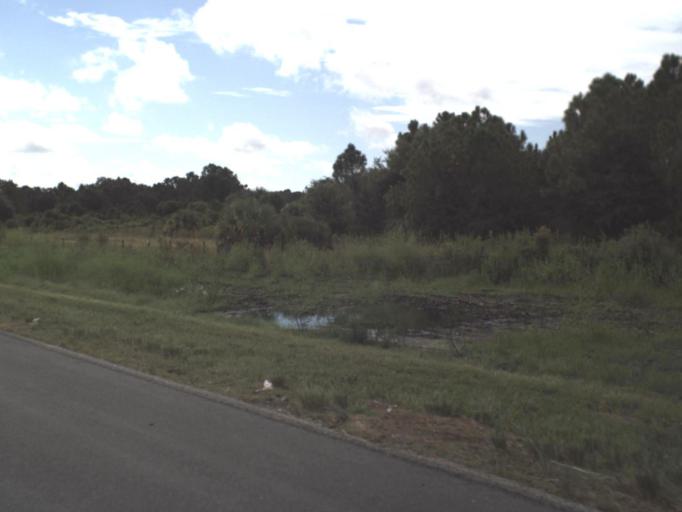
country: US
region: Florida
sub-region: Sarasota County
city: Warm Mineral Springs
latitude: 27.1083
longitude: -82.3079
